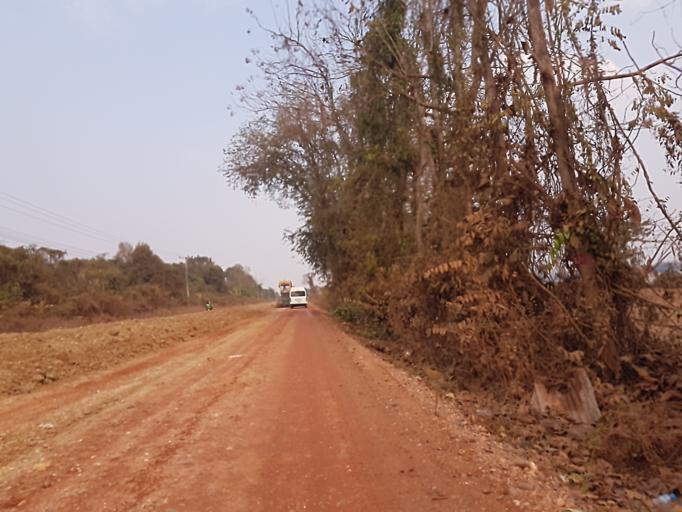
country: TH
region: Nong Khai
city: Nong Khai
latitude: 17.9786
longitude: 102.8698
